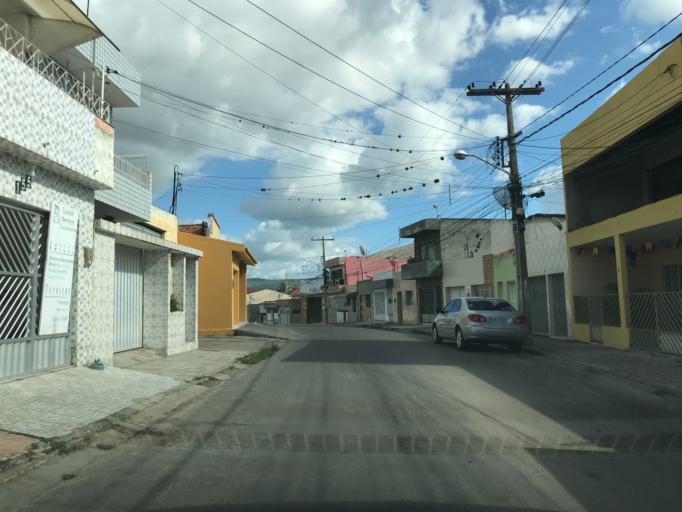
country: BR
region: Pernambuco
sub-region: Bezerros
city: Bezerros
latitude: -8.2394
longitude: -35.7542
